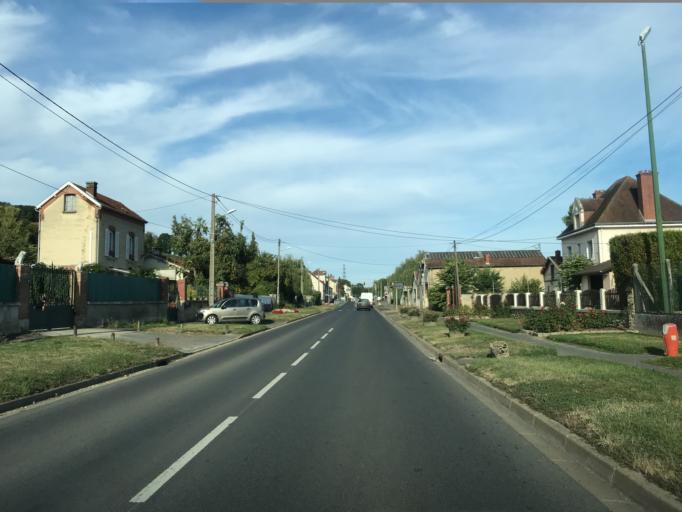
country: FR
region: Champagne-Ardenne
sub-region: Departement de la Marne
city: Damery
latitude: 49.0609
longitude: 3.8771
